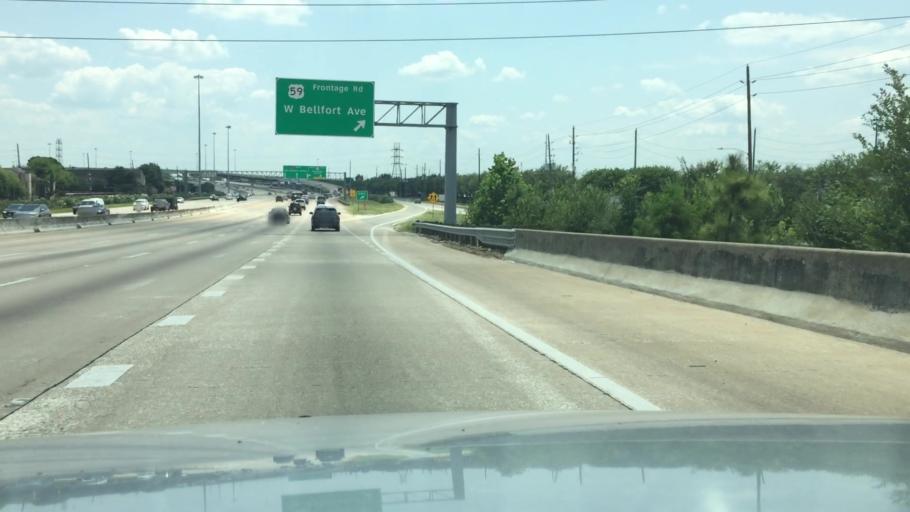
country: US
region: Texas
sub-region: Fort Bend County
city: Meadows Place
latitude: 29.6721
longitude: -95.5605
